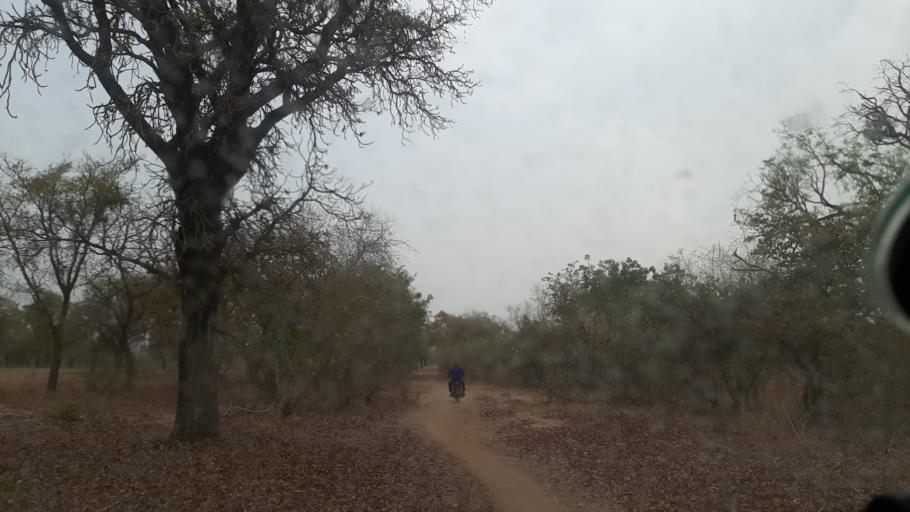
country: BF
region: Boucle du Mouhoun
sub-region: Province des Banwa
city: Salanso
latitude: 11.8572
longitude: -4.4317
